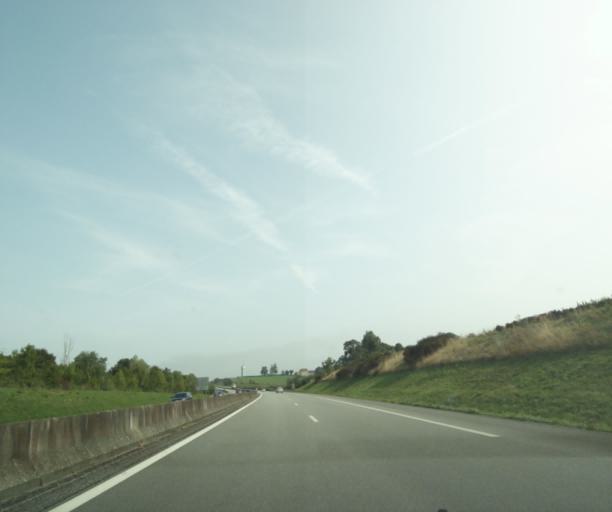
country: FR
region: Lower Normandy
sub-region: Departement de l'Orne
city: Radon
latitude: 48.5288
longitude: 0.1593
